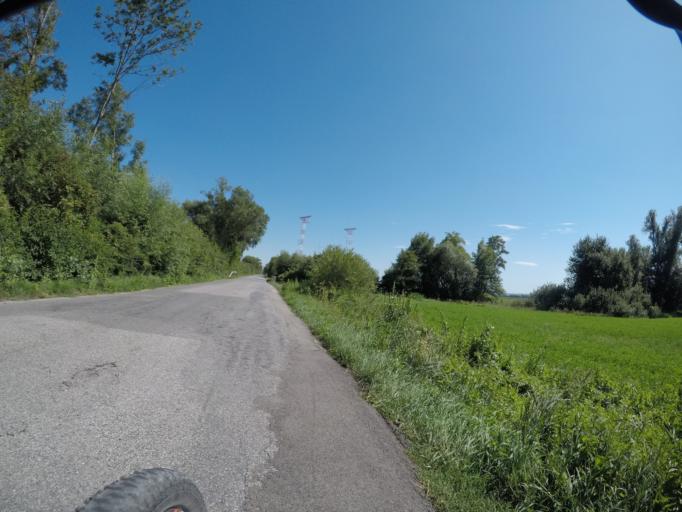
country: AT
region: Lower Austria
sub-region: Politischer Bezirk Wien-Umgebung
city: Moosbrunn
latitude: 48.0058
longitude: 16.4560
